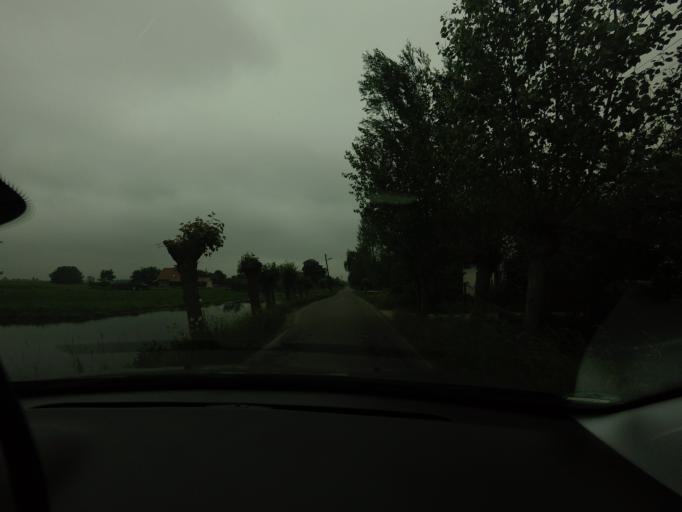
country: NL
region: South Holland
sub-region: Gemeente Vlist
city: Haastrecht
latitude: 52.0335
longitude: 4.7992
